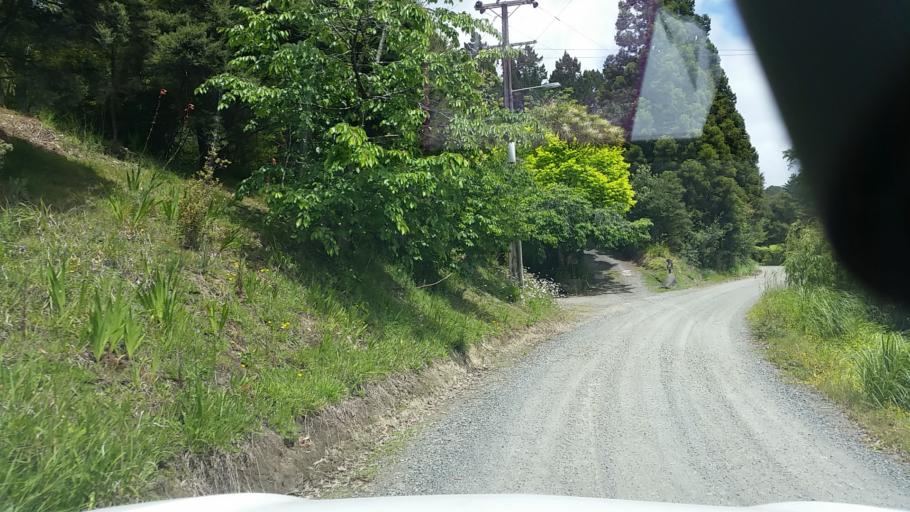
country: NZ
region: Auckland
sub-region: Auckland
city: Rosebank
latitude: -36.8529
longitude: 174.5891
